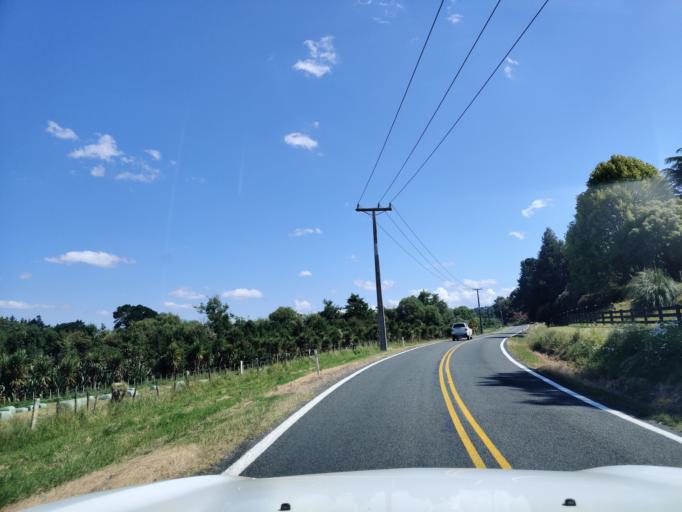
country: NZ
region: Waikato
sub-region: Waikato District
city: Ngaruawahia
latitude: -37.6492
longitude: 175.1454
